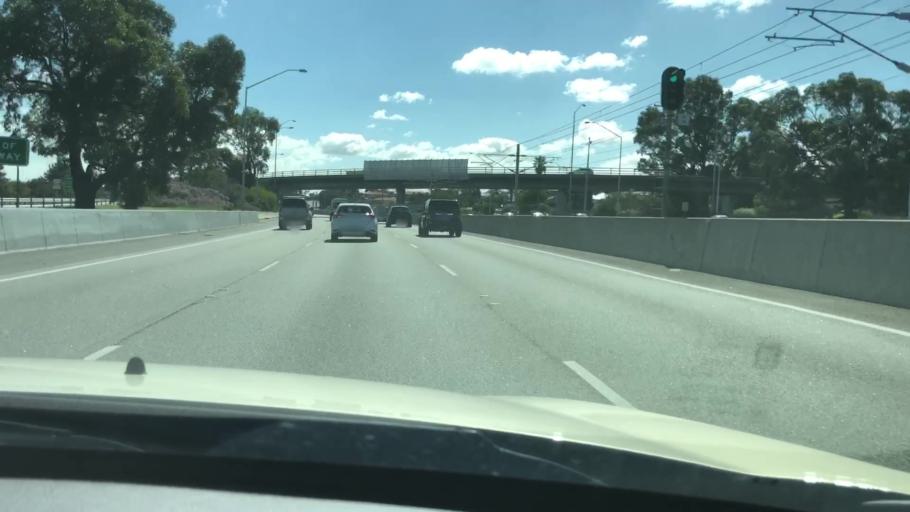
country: AU
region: Western Australia
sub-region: South Perth
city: Manning
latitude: -32.0148
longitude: 115.8576
